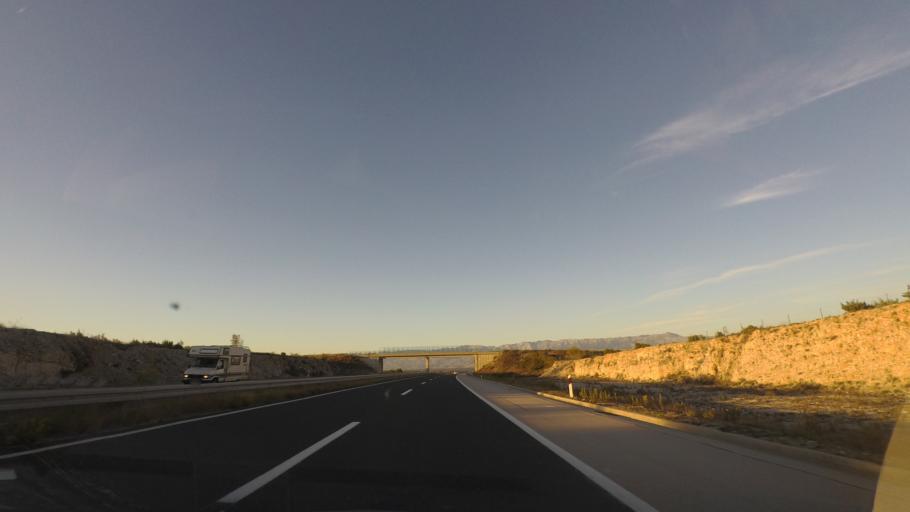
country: HR
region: Zadarska
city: Policnik
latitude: 44.1396
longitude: 15.4203
